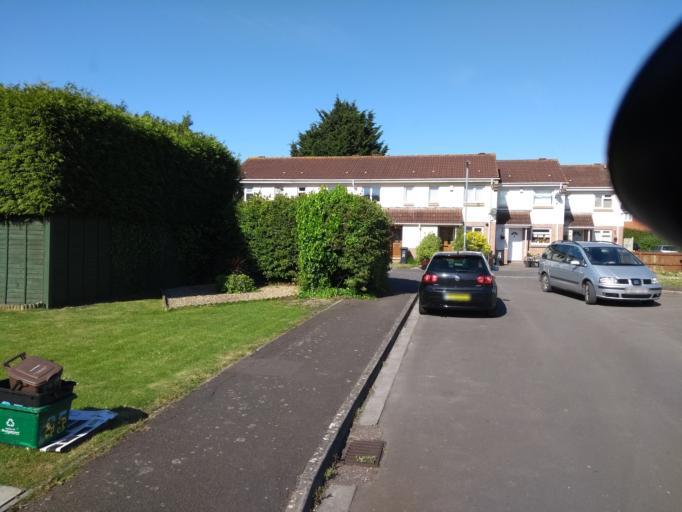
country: GB
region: England
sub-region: Somerset
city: Bridgwater
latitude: 51.1369
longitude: -3.0085
